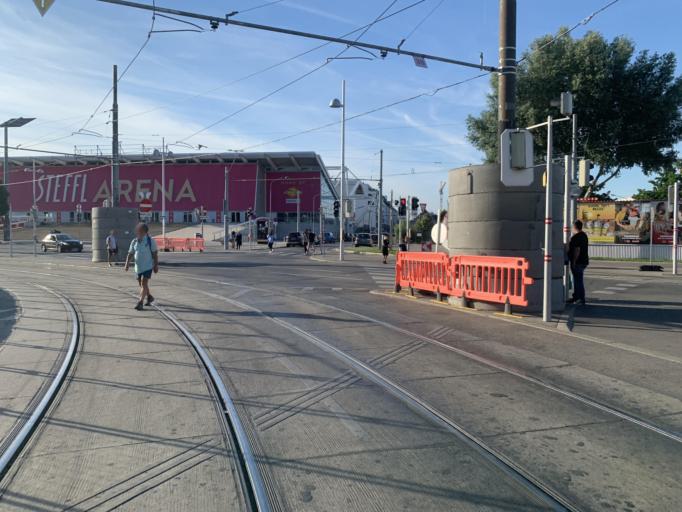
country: AT
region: Lower Austria
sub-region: Politischer Bezirk Wien-Umgebung
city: Gerasdorf bei Wien
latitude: 48.2448
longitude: 16.4343
